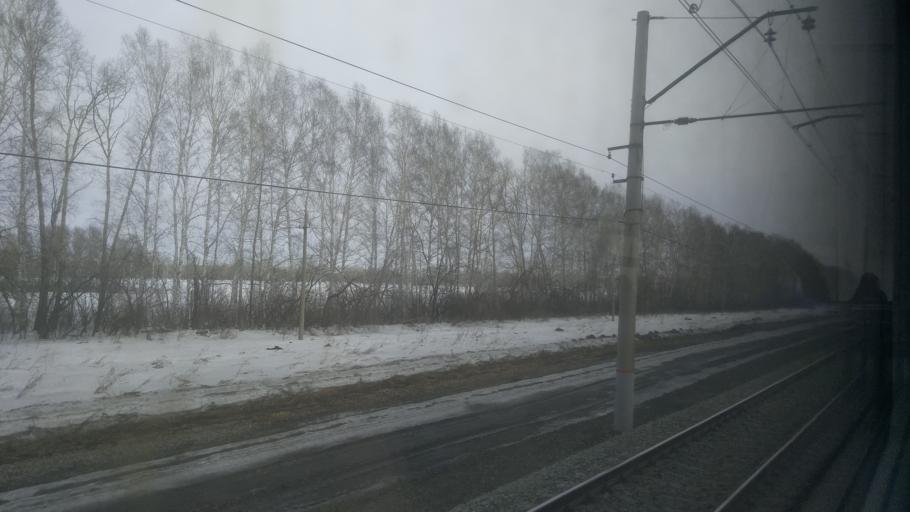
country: RU
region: Novosibirsk
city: Bolotnoye
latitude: 55.7063
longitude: 84.5988
